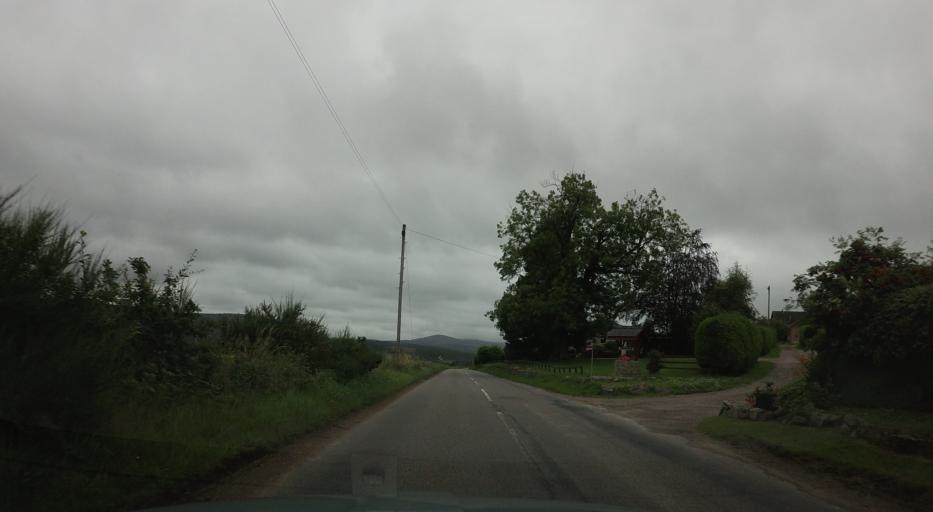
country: GB
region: Scotland
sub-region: Aberdeenshire
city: Banchory
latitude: 57.0270
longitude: -2.5180
